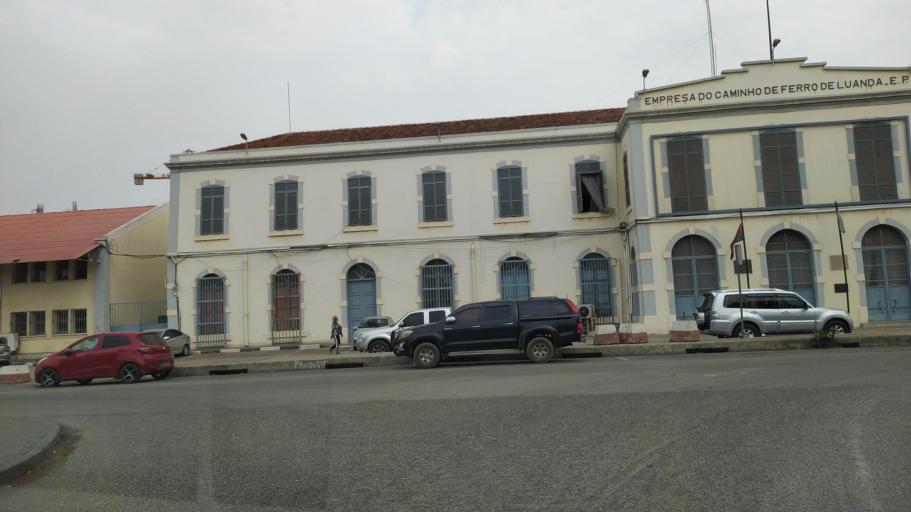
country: AO
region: Luanda
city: Luanda
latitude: -8.8050
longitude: 13.2441
